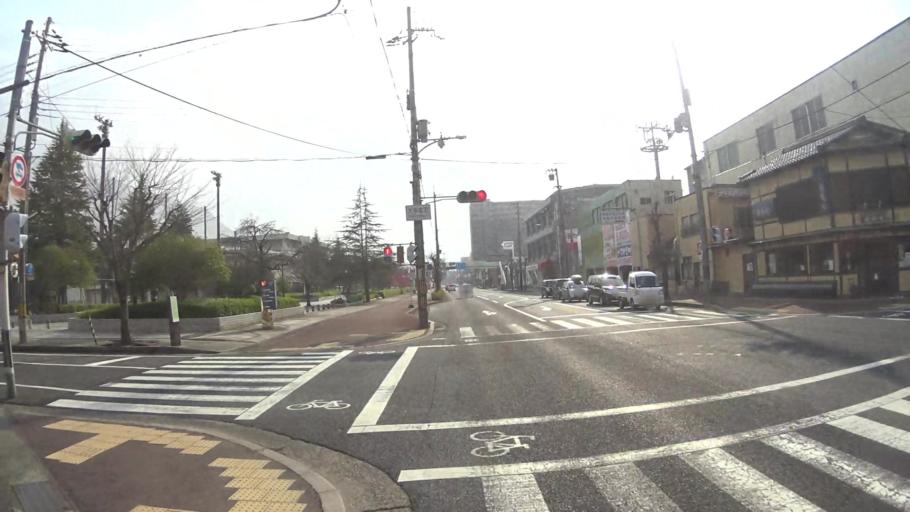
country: JP
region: Kyoto
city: Maizuru
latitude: 35.4482
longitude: 135.3289
